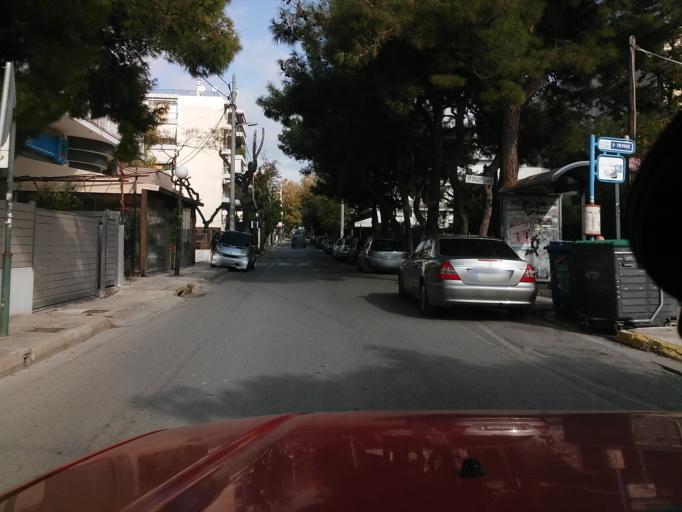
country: GR
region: Attica
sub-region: Nomarchia Athinas
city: Irakleio
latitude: 38.0568
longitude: 23.7737
